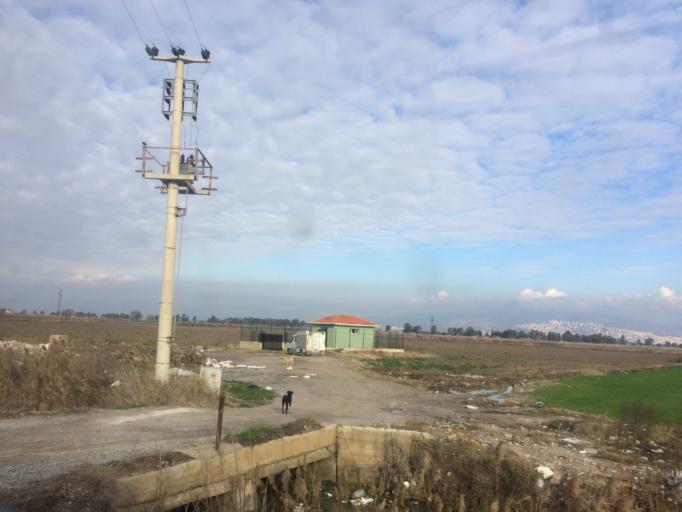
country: TR
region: Izmir
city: Karsiyaka
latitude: 38.4957
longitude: 26.9603
